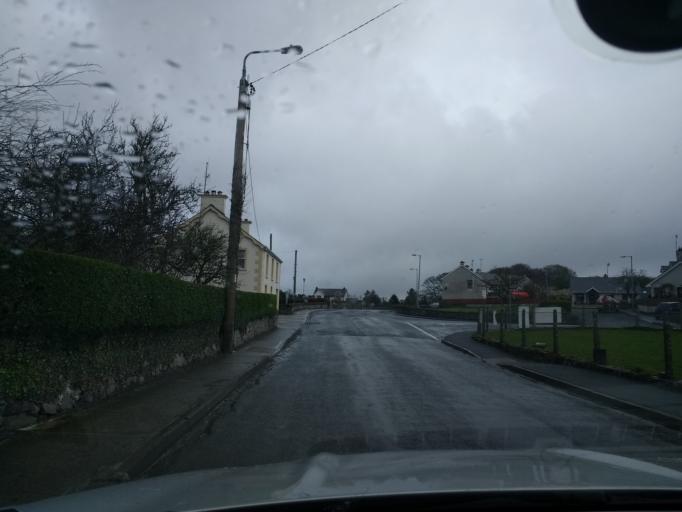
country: IE
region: Ulster
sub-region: County Donegal
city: Buncrana
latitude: 55.0960
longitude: -7.5369
